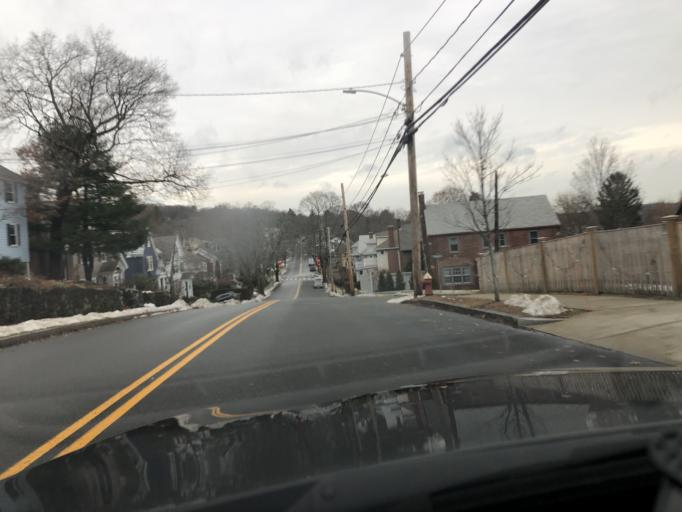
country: US
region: Massachusetts
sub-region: Middlesex County
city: Arlington
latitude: 42.4143
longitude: -71.1668
